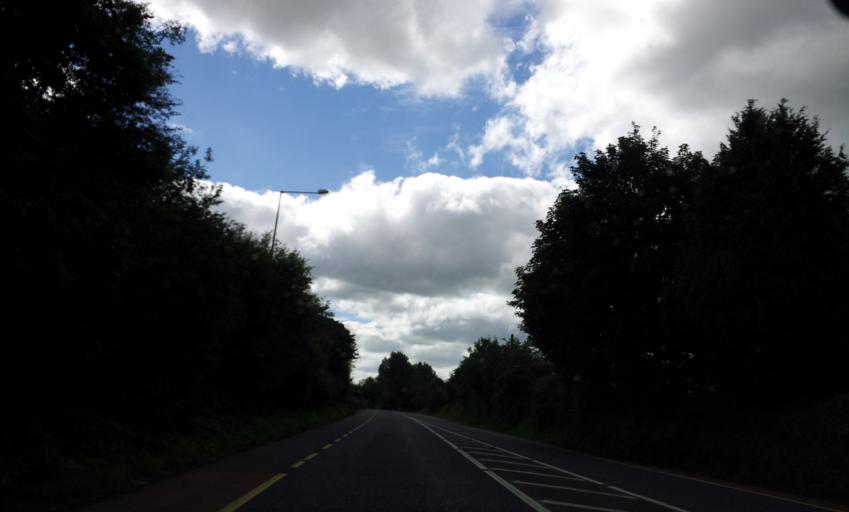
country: IE
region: Munster
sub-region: County Cork
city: Killumney
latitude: 51.8823
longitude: -8.6790
